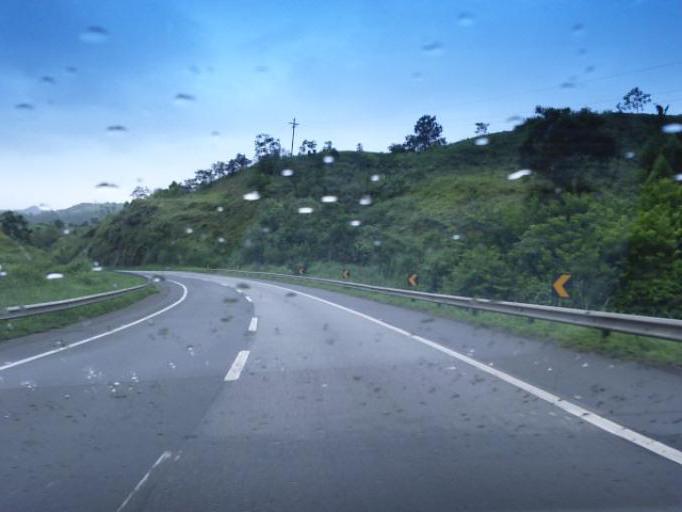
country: BR
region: Sao Paulo
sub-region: Cajati
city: Cajati
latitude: -24.8298
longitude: -48.2091
